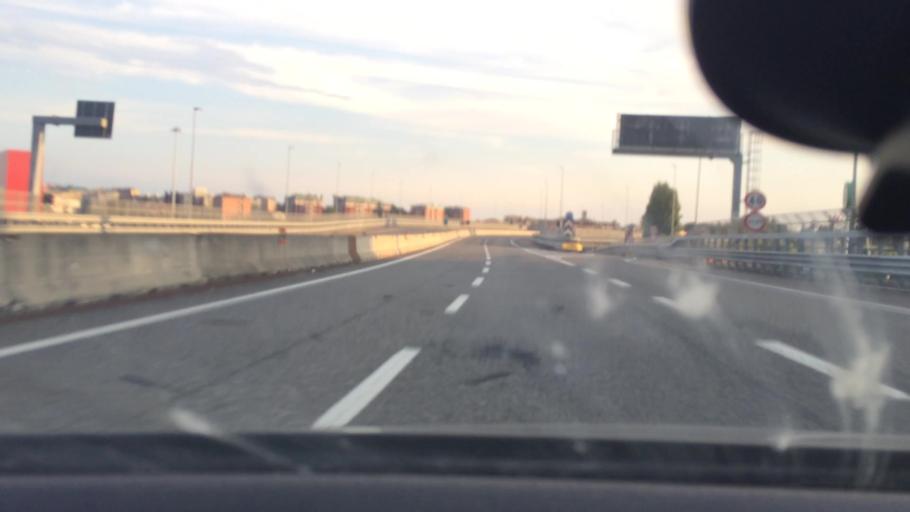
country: IT
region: Lombardy
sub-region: Citta metropolitana di Milano
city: Pero
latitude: 45.5185
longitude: 9.0878
